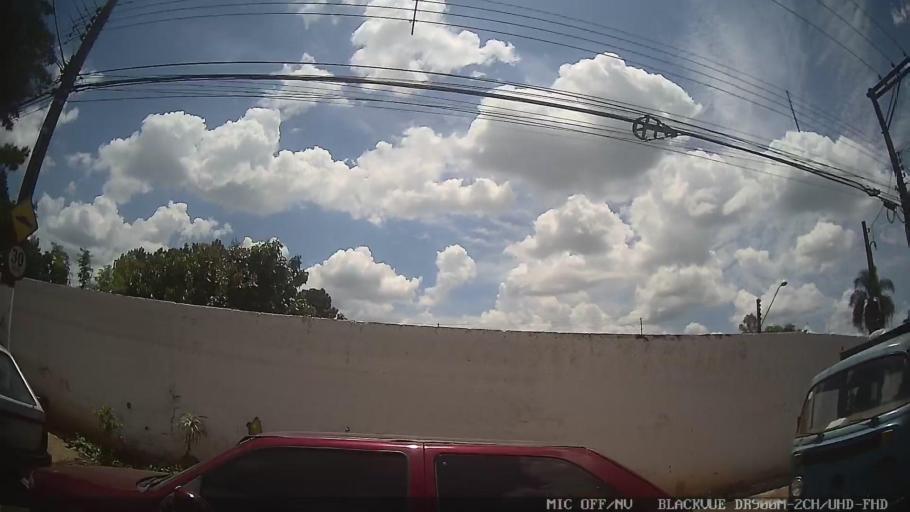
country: BR
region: Sao Paulo
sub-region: Atibaia
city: Atibaia
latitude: -23.1147
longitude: -46.5853
